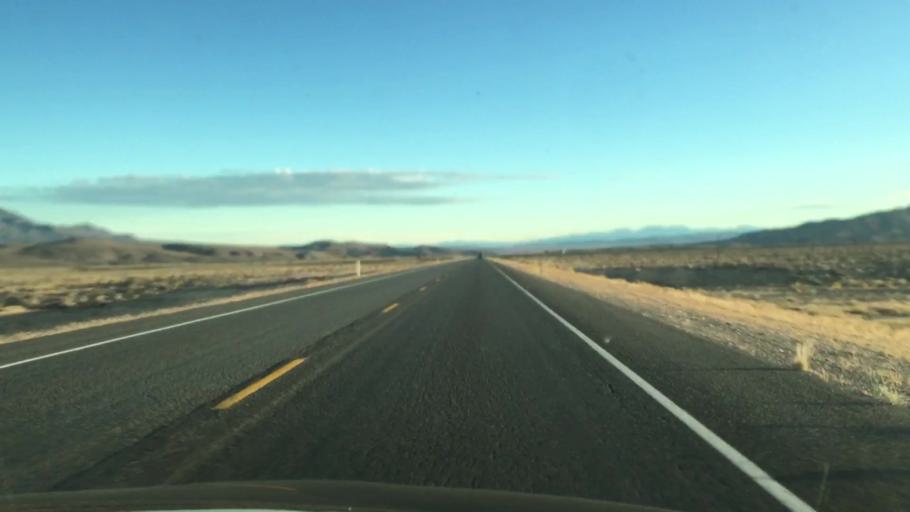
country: US
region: Nevada
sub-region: Esmeralda County
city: Goldfield
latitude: 37.5967
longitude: -117.2109
